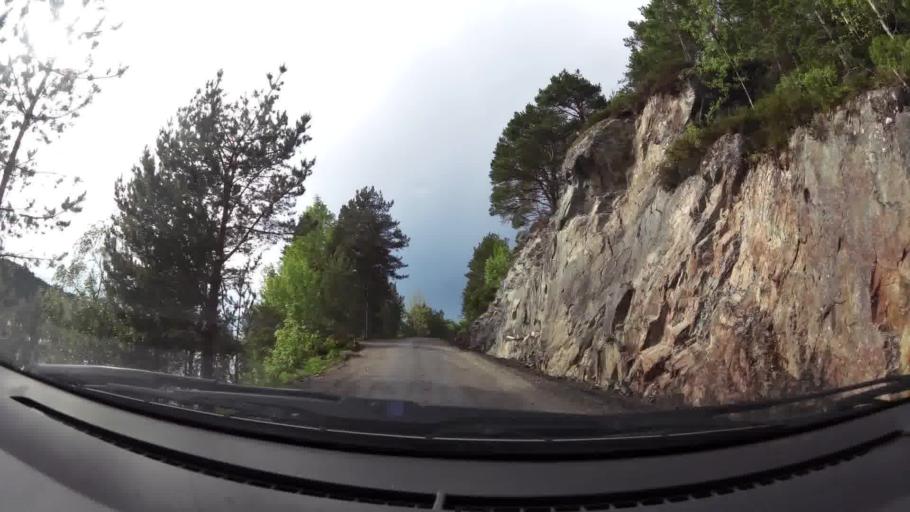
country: NO
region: More og Romsdal
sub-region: Kristiansund
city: Kristiansund
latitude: 63.0534
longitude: 7.7270
